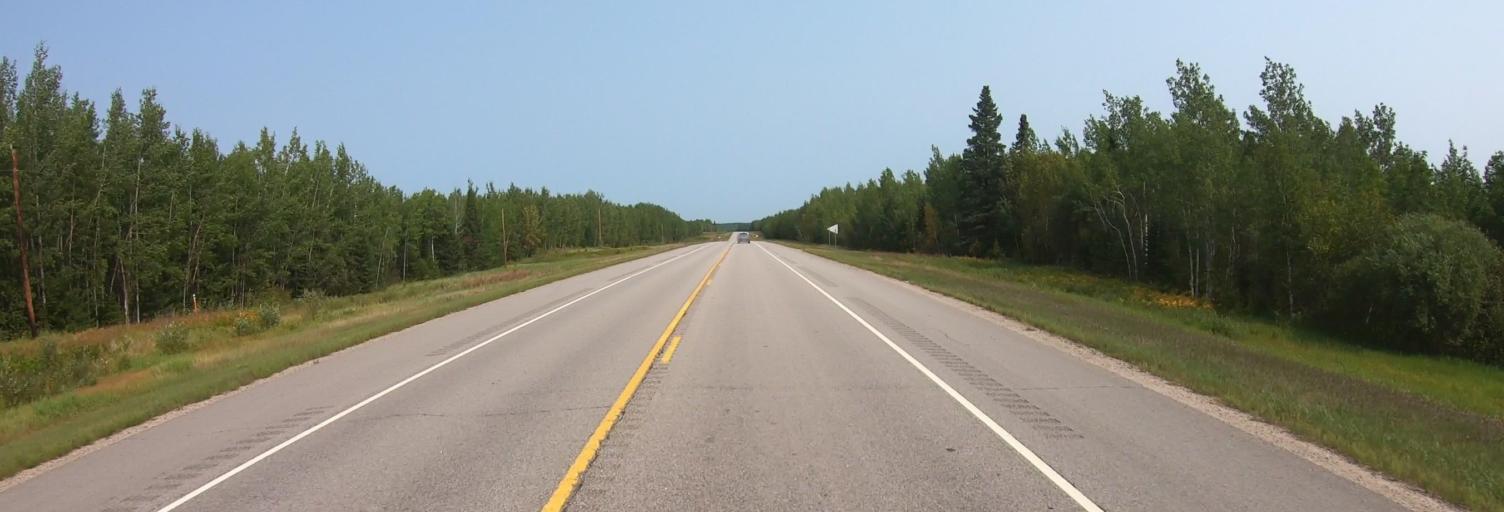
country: CA
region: Ontario
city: Fort Frances
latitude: 48.3011
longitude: -92.9693
